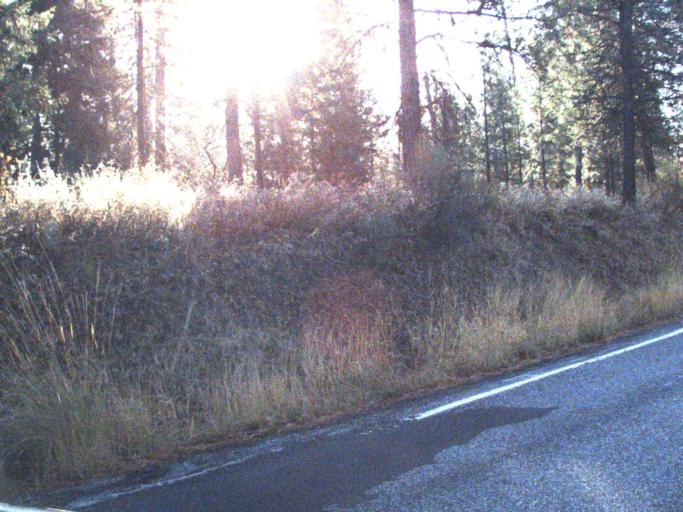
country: US
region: Washington
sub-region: Okanogan County
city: Coulee Dam
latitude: 48.0534
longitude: -118.6701
